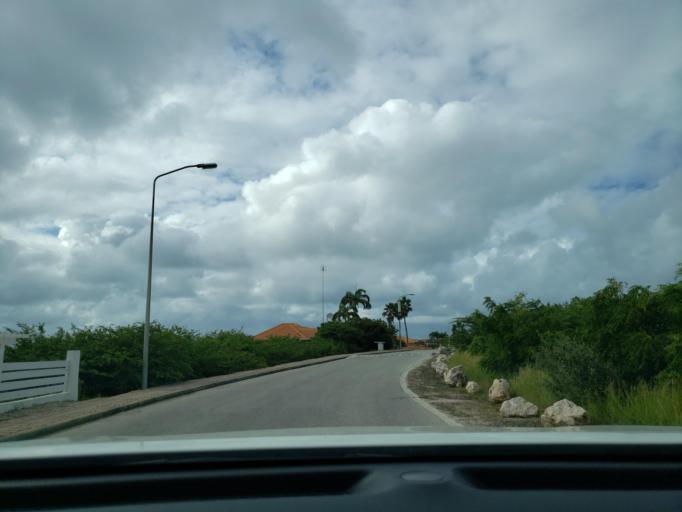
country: CW
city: Dorp Soto
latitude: 12.1967
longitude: -69.0752
